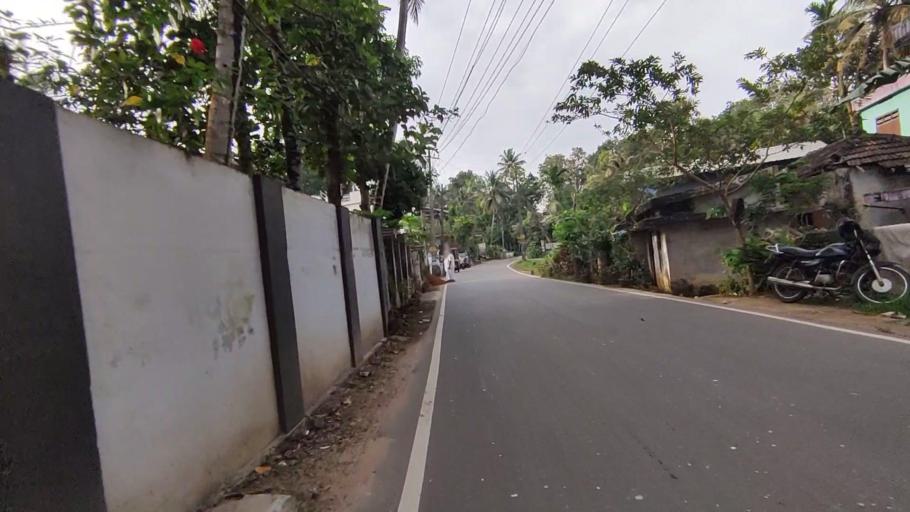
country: IN
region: Kerala
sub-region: Kottayam
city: Kottayam
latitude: 9.5993
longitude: 76.5037
